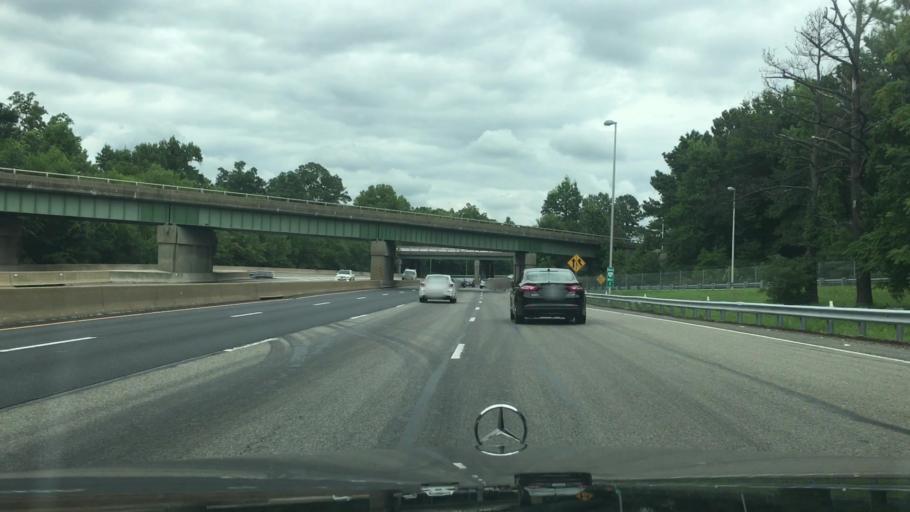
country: US
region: Virginia
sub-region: Chesterfield County
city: Bon Air
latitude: 37.5327
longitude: -77.5098
